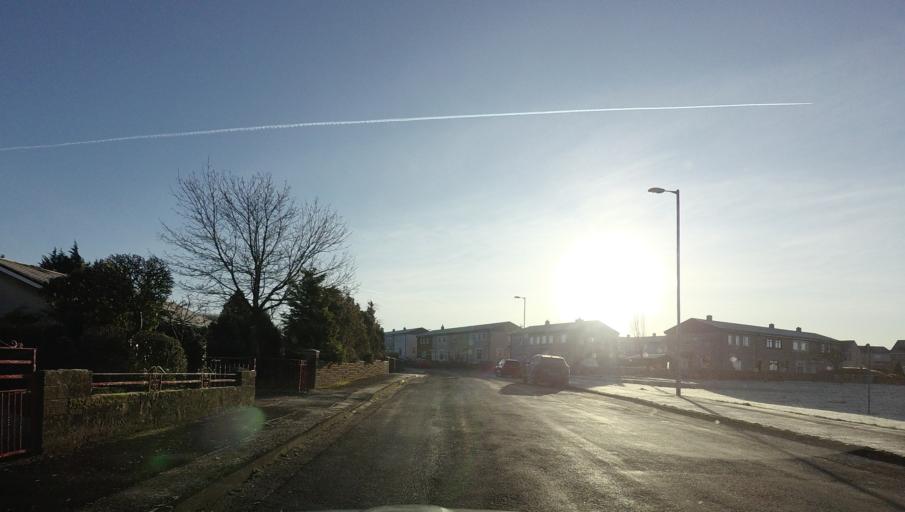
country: GB
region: Scotland
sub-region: North Lanarkshire
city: Shotts
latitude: 55.8011
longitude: -3.8238
